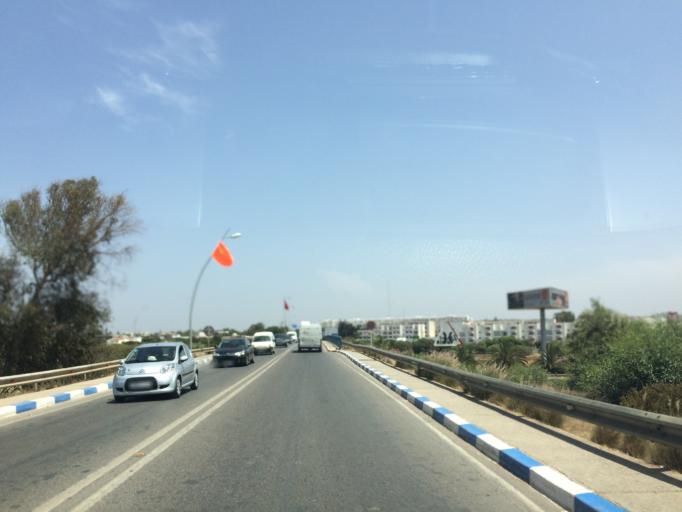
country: MA
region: Rabat-Sale-Zemmour-Zaer
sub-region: Skhirate-Temara
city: Temara
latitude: 33.9332
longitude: -6.9379
